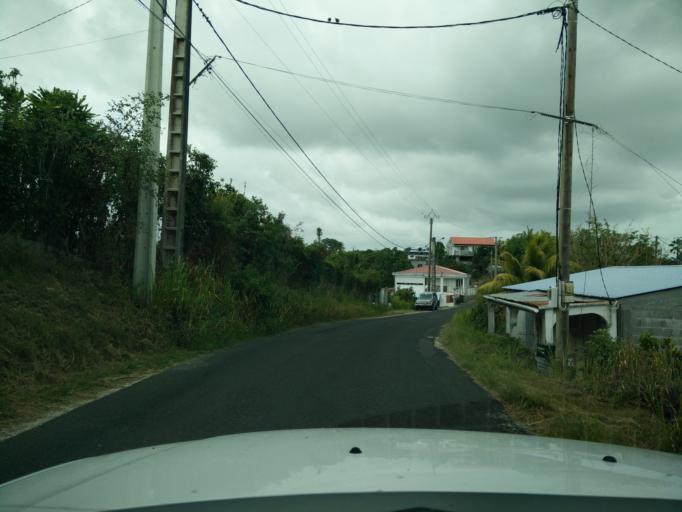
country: GP
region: Guadeloupe
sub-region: Guadeloupe
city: Le Gosier
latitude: 16.2366
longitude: -61.4525
